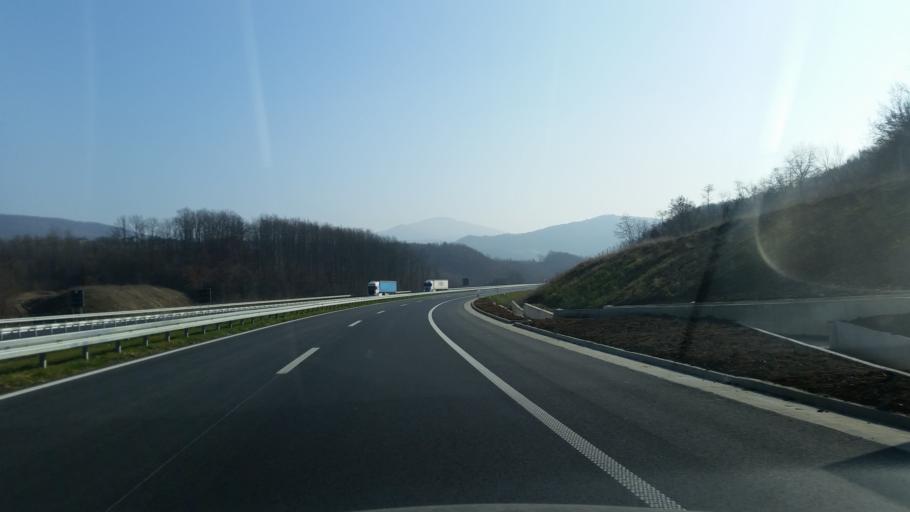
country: RS
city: Prislonica
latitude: 44.0117
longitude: 20.3821
